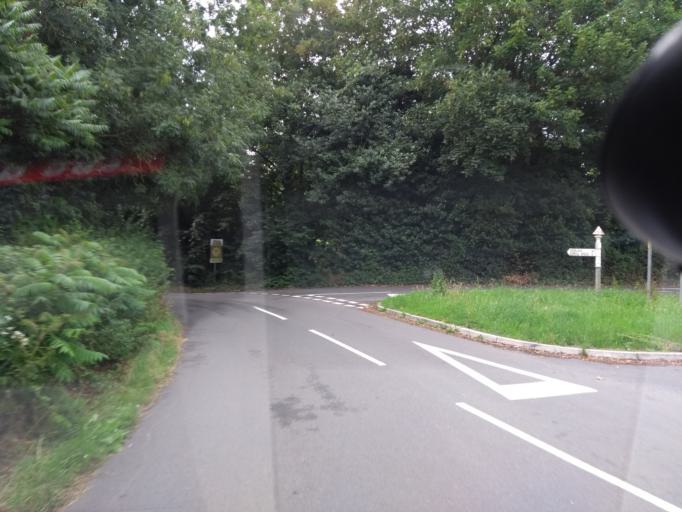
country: GB
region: England
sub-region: Somerset
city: Bridgwater
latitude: 51.1045
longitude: -2.9837
